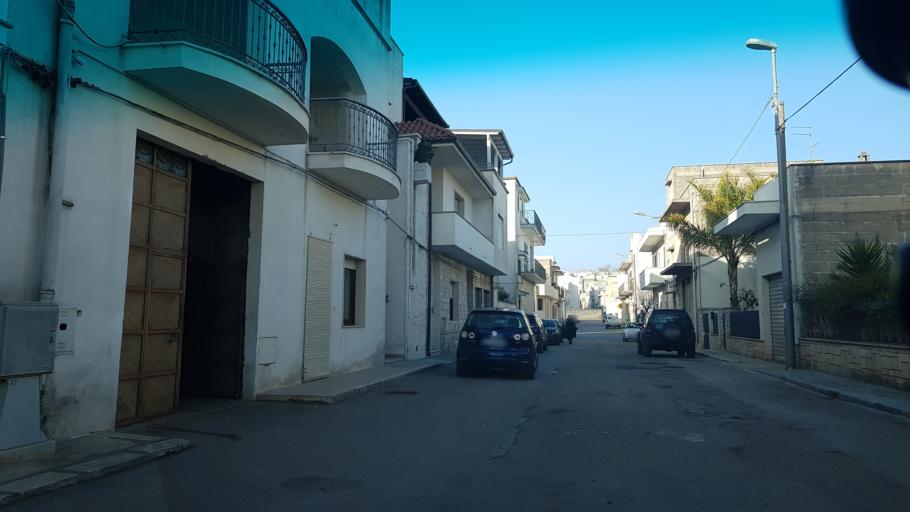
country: IT
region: Apulia
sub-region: Provincia di Brindisi
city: Carovigno
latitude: 40.7014
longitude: 17.6555
